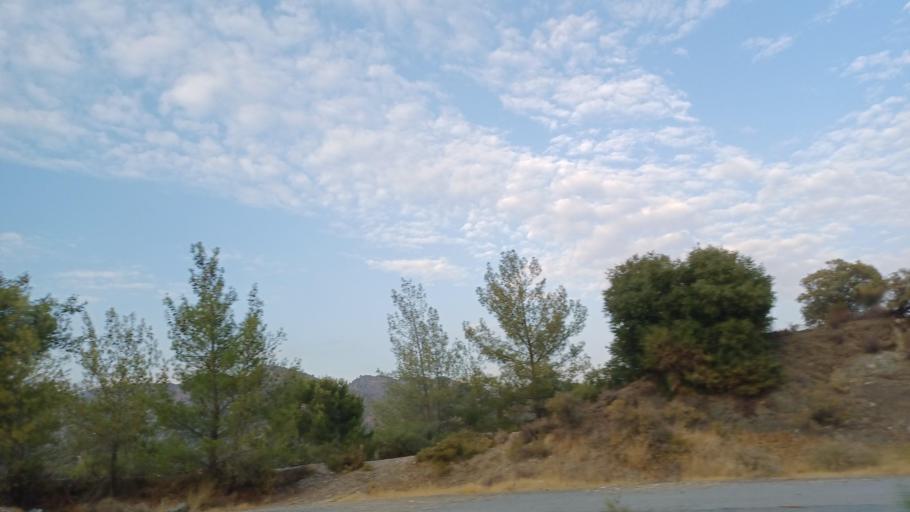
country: CY
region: Limassol
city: Pelendri
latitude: 34.8571
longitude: 32.9387
